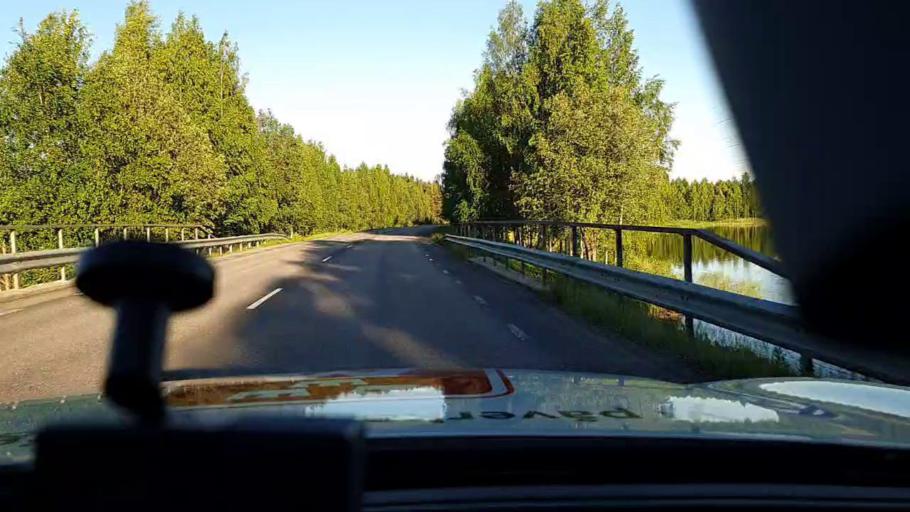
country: SE
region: Norrbotten
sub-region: Lulea Kommun
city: Lulea
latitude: 65.6121
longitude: 22.1613
